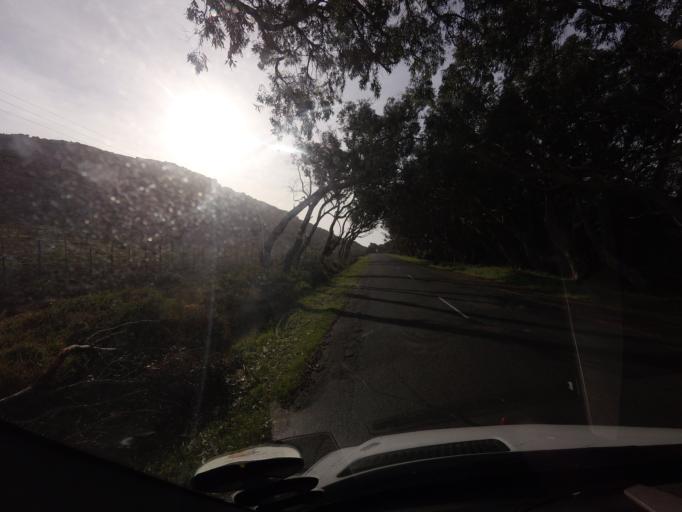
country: ZA
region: Western Cape
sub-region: City of Cape Town
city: Retreat
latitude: -34.2528
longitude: 18.4434
